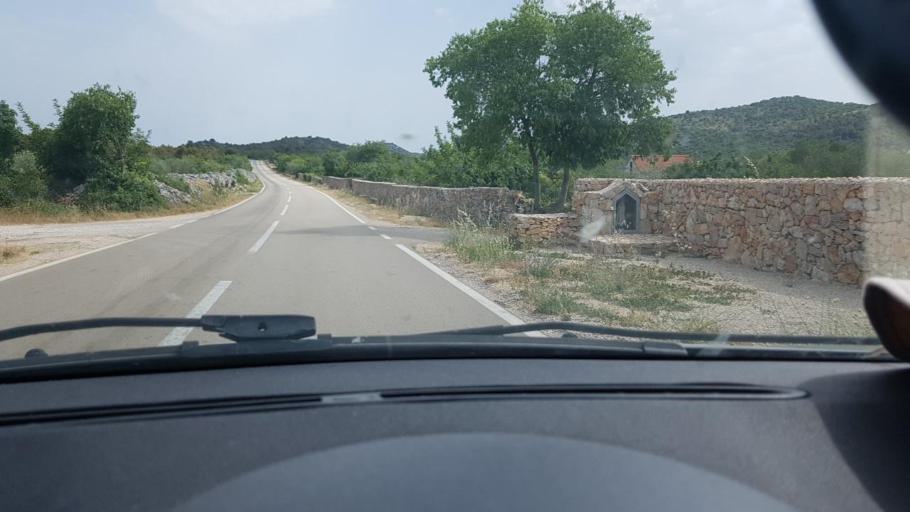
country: HR
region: Sibensko-Kniniska
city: Zaton
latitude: 43.8145
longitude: 15.7776
